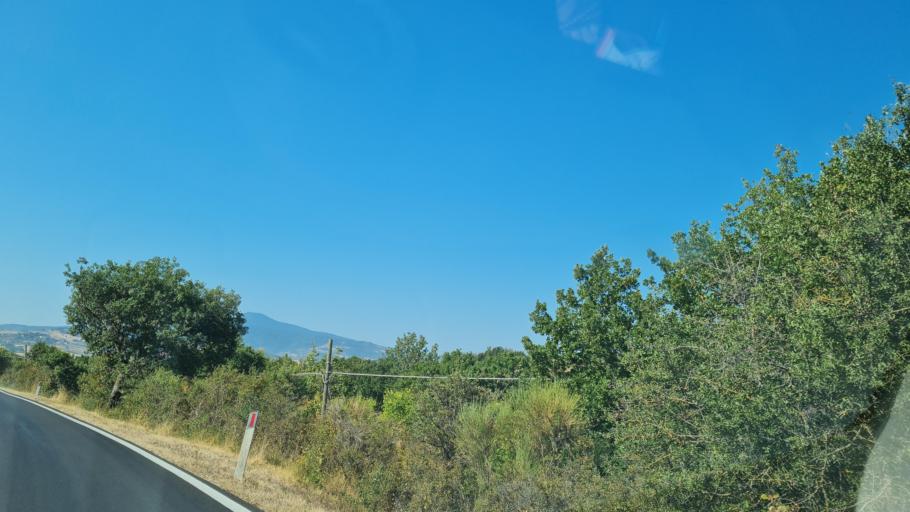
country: IT
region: Tuscany
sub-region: Provincia di Siena
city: Chianciano Terme
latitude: 43.0172
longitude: 11.7655
